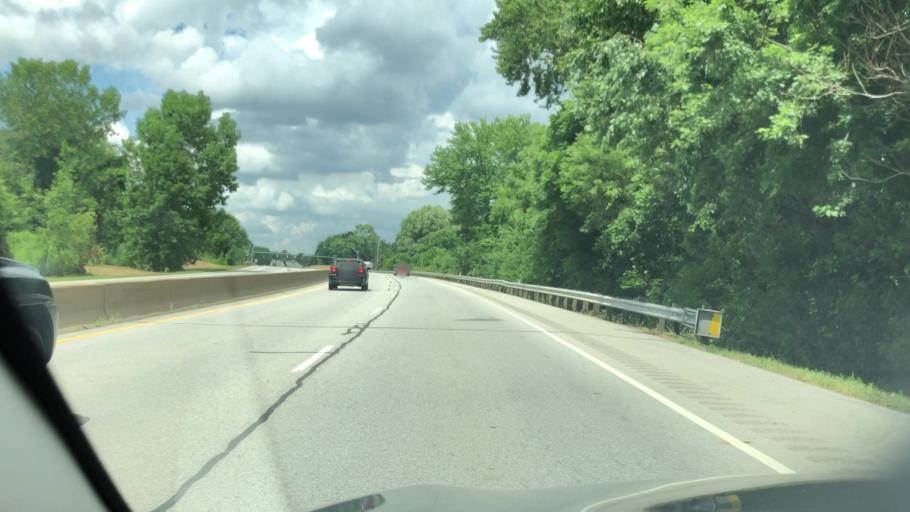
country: US
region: Ohio
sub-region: Stark County
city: Massillon
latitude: 40.8090
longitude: -81.5260
